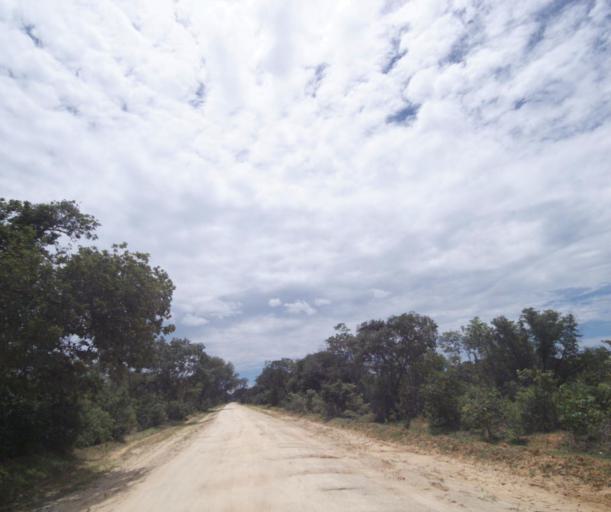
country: BR
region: Bahia
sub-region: Carinhanha
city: Carinhanha
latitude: -14.2102
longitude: -43.9098
